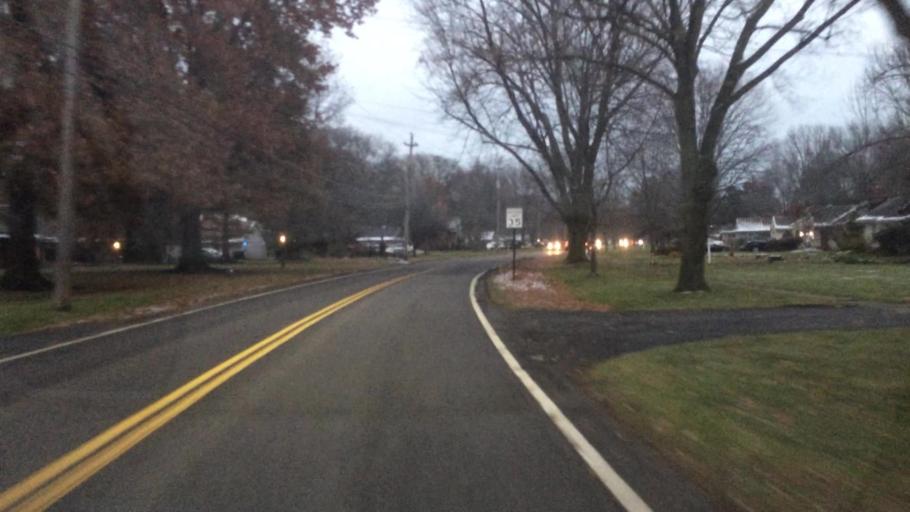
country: US
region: Ohio
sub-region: Cuyahoga County
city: Berea
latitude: 41.3655
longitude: -81.8804
